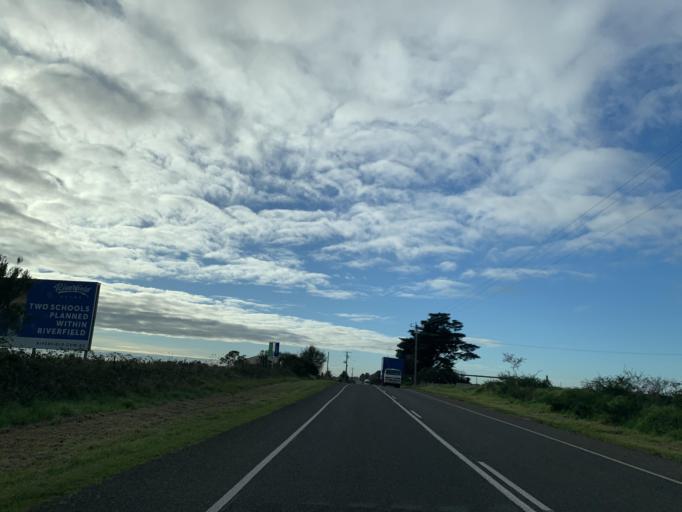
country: AU
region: Victoria
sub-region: Casey
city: Junction Village
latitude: -38.1367
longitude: 145.3508
